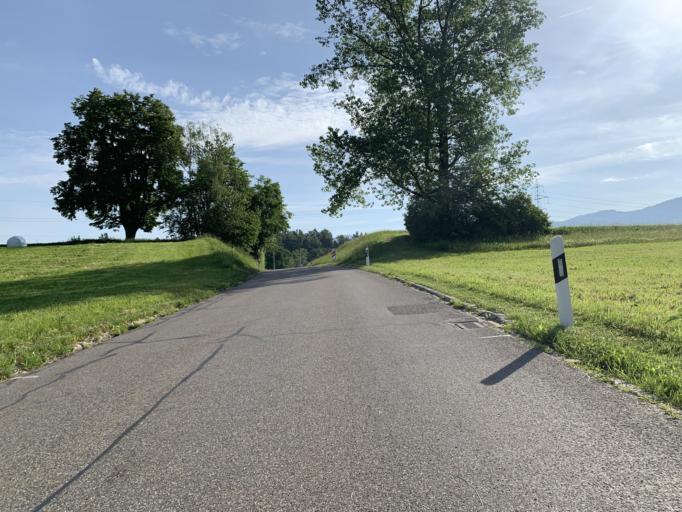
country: CH
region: Zurich
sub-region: Bezirk Hinwil
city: Wetzikon / Unter-Wetzikon
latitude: 47.2936
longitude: 8.8093
